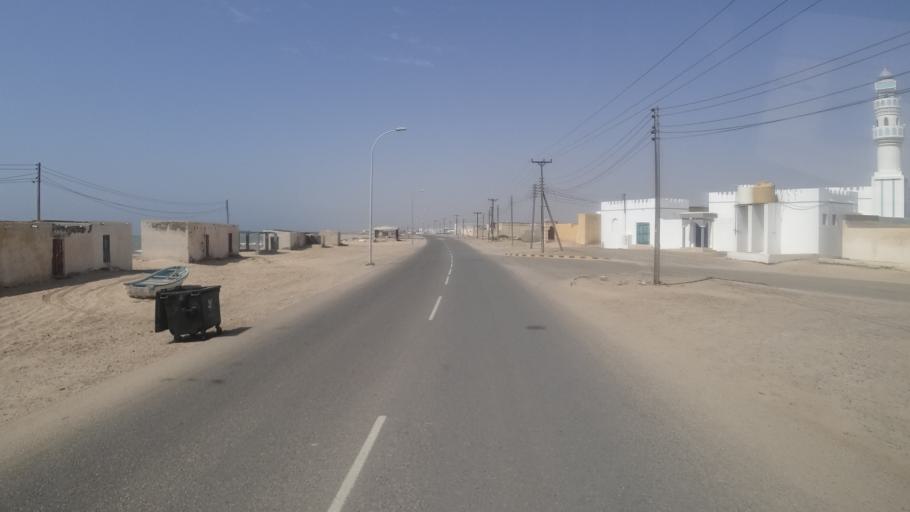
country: OM
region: Ash Sharqiyah
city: Sur
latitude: 22.1170
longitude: 59.7143
